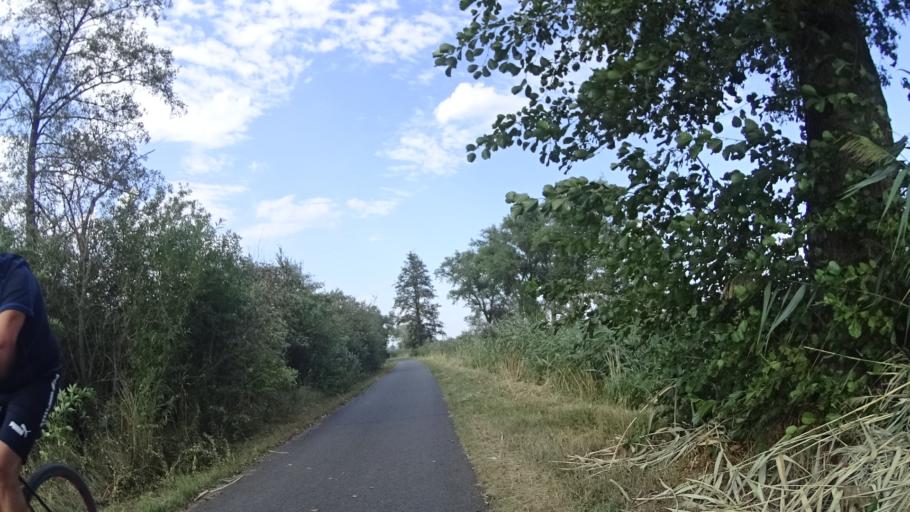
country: CZ
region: Zlin
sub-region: Okres Uherske Hradiste
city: Uherske Hradiste
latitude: 49.0901
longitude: 17.4723
